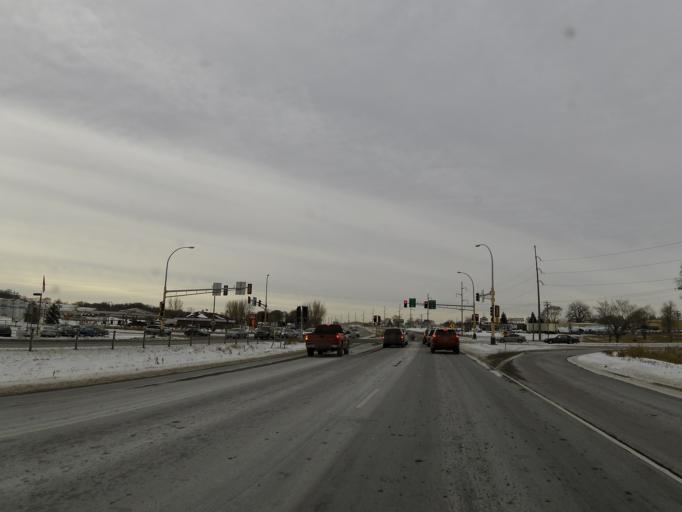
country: US
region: Minnesota
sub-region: Carver County
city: Chaska
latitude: 44.7664
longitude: -93.5780
